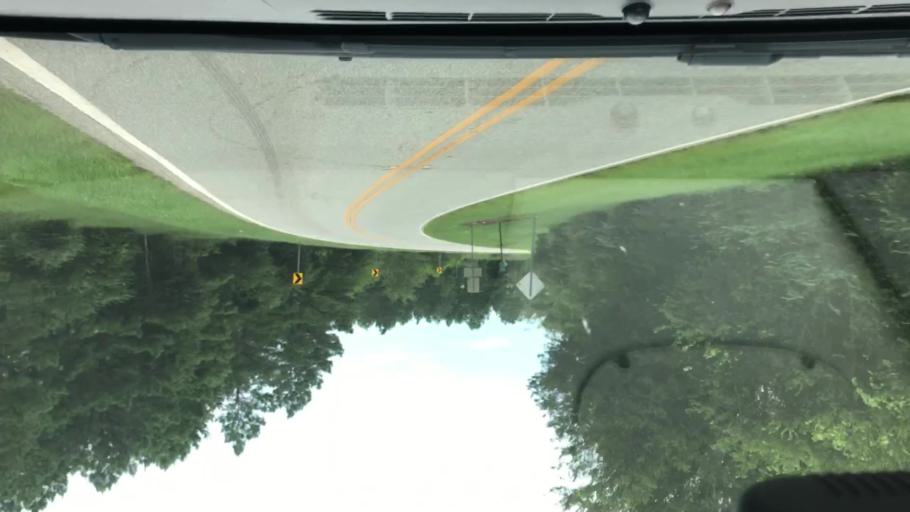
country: US
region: Georgia
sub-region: Early County
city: Blakely
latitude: 31.4099
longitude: -84.9251
